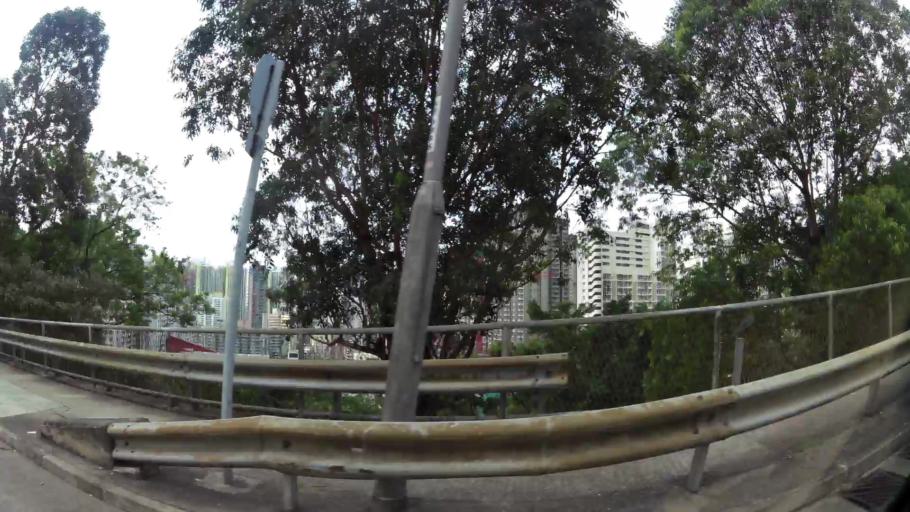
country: HK
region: Sham Shui Po
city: Sham Shui Po
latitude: 22.3417
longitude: 114.1598
